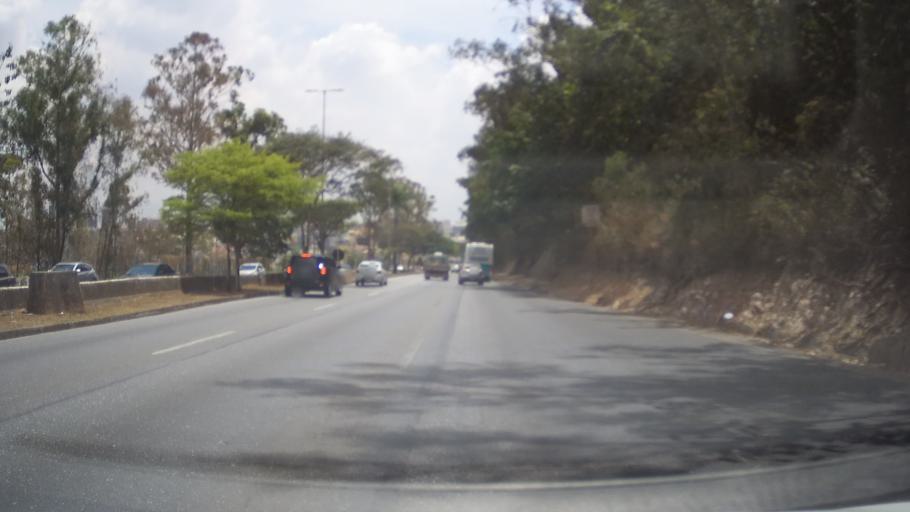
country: BR
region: Minas Gerais
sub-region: Belo Horizonte
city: Belo Horizonte
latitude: -19.9628
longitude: -43.9412
